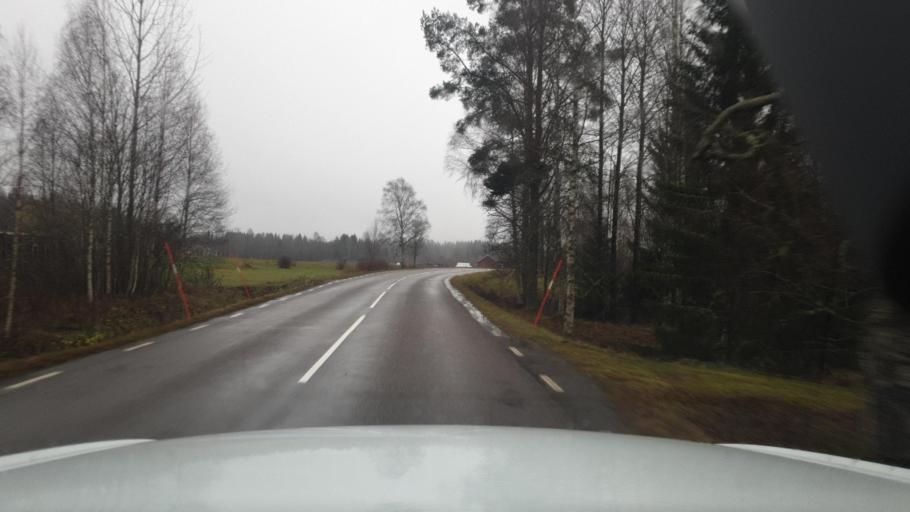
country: SE
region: Vaermland
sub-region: Sunne Kommun
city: Sunne
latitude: 59.7976
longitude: 13.0663
